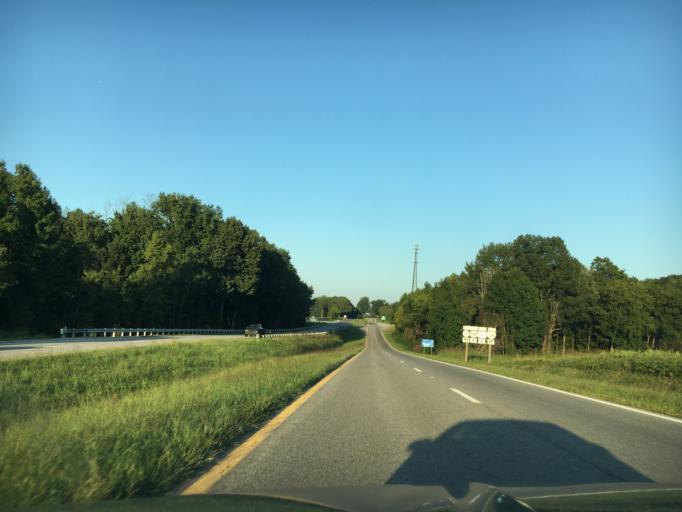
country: US
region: Virginia
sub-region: Halifax County
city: Mountain Road
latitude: 36.5840
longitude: -79.1439
